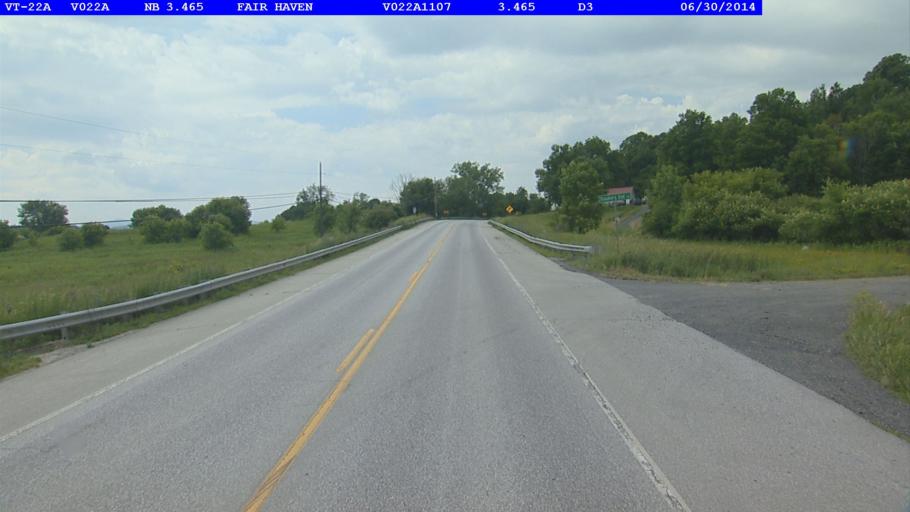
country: US
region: Vermont
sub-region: Rutland County
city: Fair Haven
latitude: 43.6152
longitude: -73.2921
